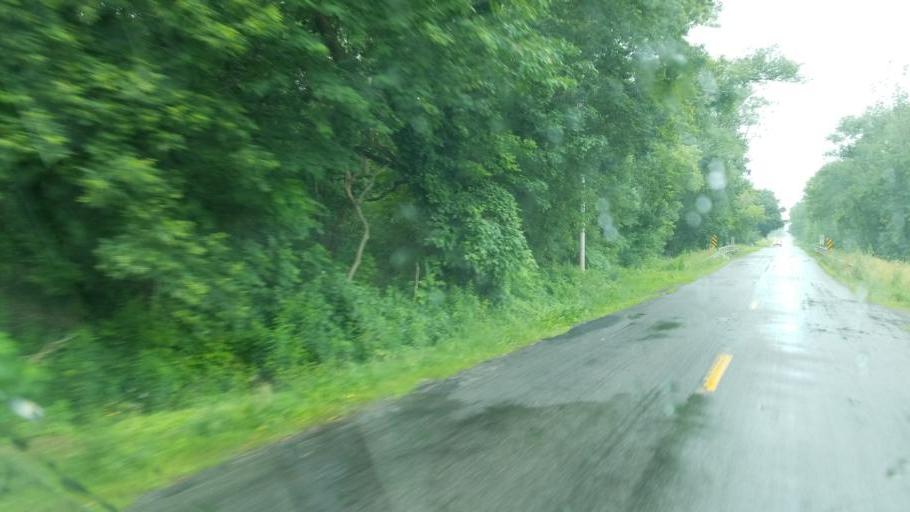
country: US
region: New York
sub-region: Niagara County
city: Wilson
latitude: 43.2644
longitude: -78.8415
